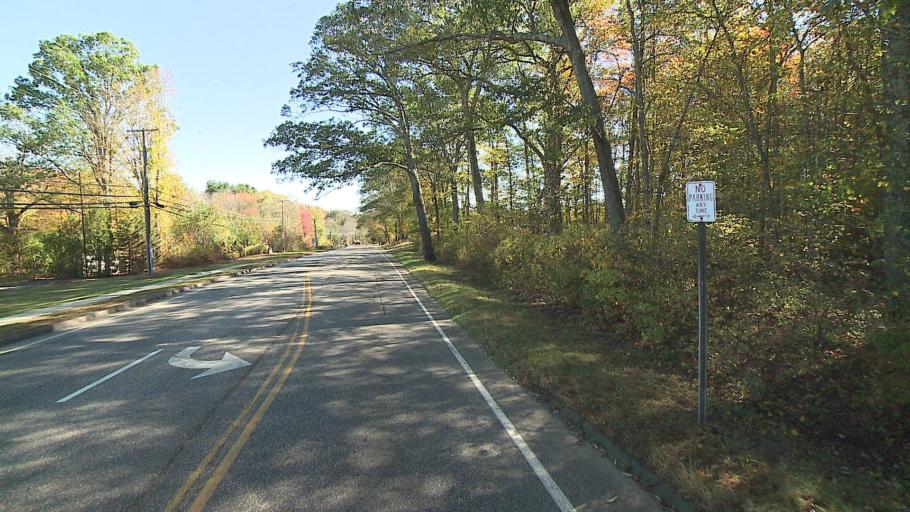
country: US
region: Connecticut
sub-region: Tolland County
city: Hebron
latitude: 41.6609
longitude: -72.3551
